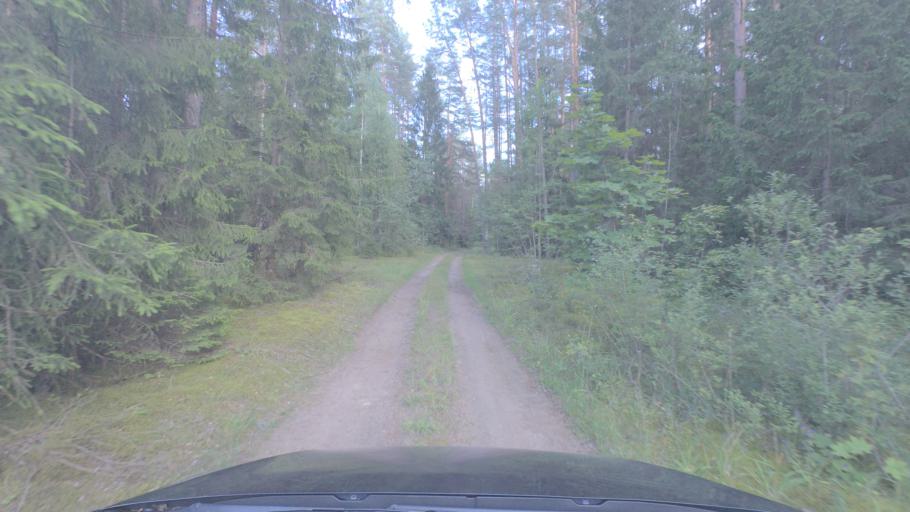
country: LT
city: Svencioneliai
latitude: 55.1614
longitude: 25.8508
